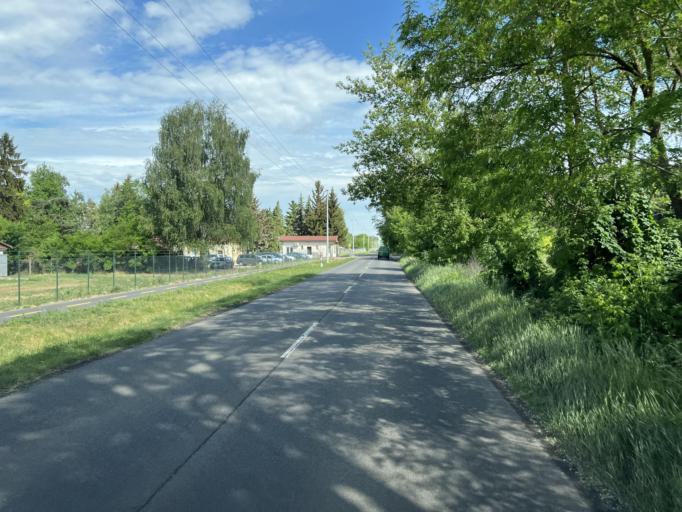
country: HU
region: Pest
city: Godollo
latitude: 47.5661
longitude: 19.3737
